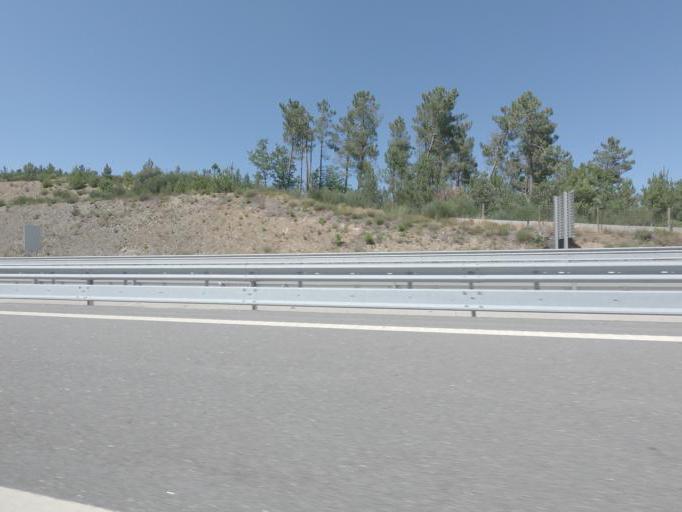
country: PT
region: Vila Real
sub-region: Santa Marta de Penaguiao
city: Santa Marta de Penaguiao
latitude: 41.2776
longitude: -7.8241
